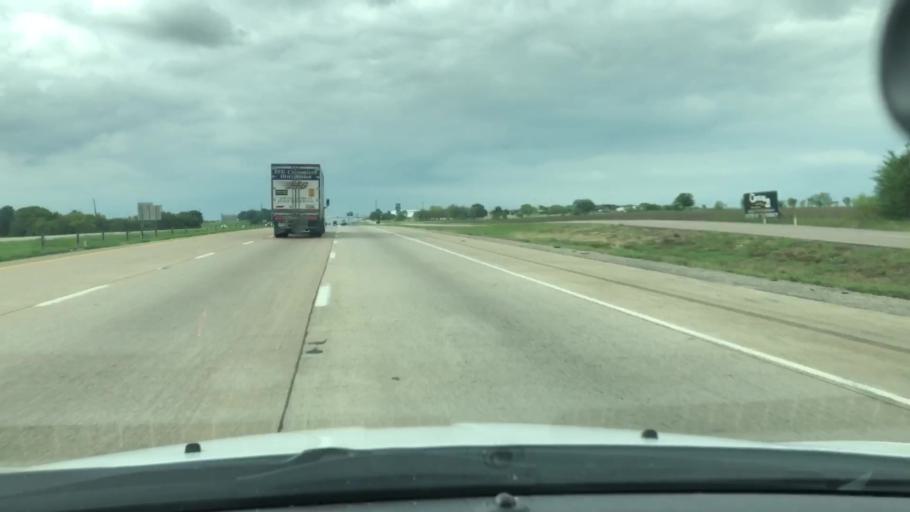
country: US
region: Texas
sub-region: Ellis County
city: Ennis
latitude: 32.3440
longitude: -96.6204
